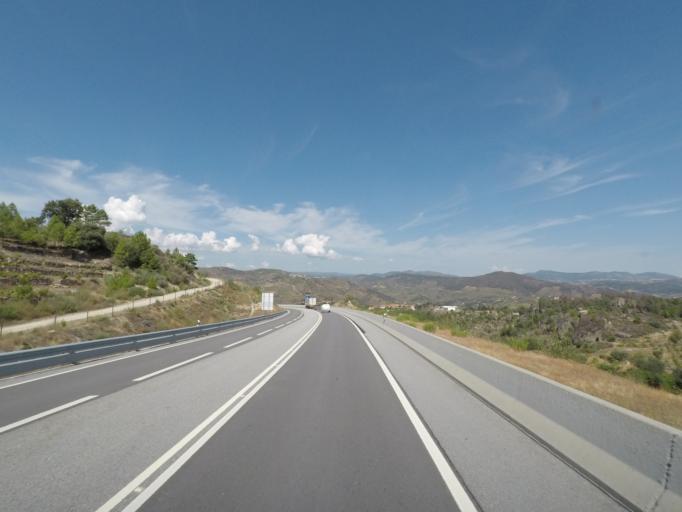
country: PT
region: Braganca
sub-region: Carrazeda de Ansiaes
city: Carrazeda de Anciaes
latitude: 41.3136
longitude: -7.3486
